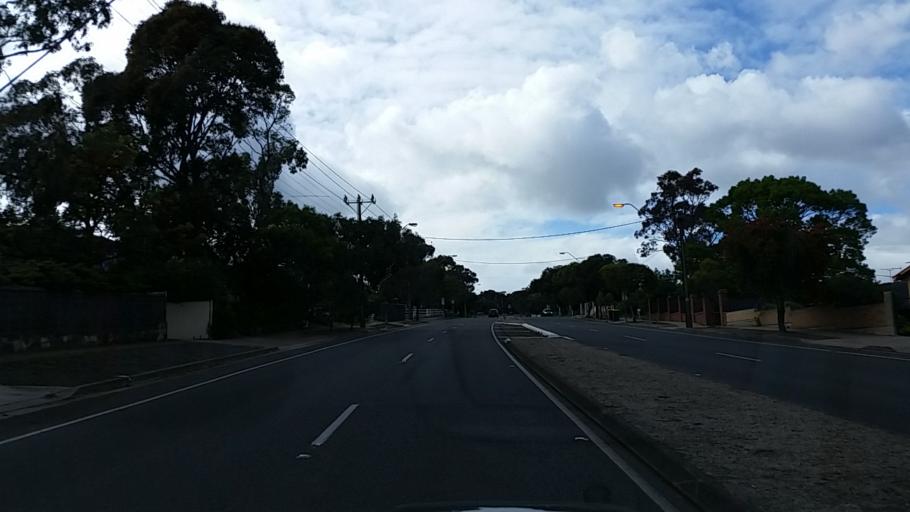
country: AU
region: South Australia
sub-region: Marion
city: Marion
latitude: -35.0218
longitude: 138.5838
